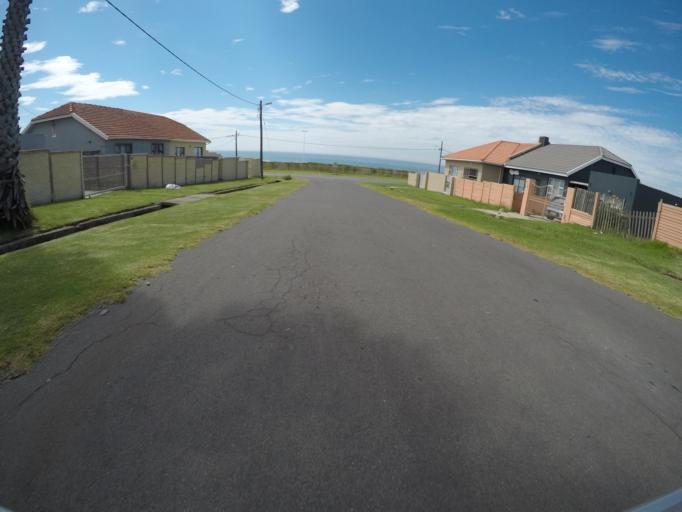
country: ZA
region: Eastern Cape
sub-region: Buffalo City Metropolitan Municipality
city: East London
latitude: -33.0381
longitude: 27.9054
